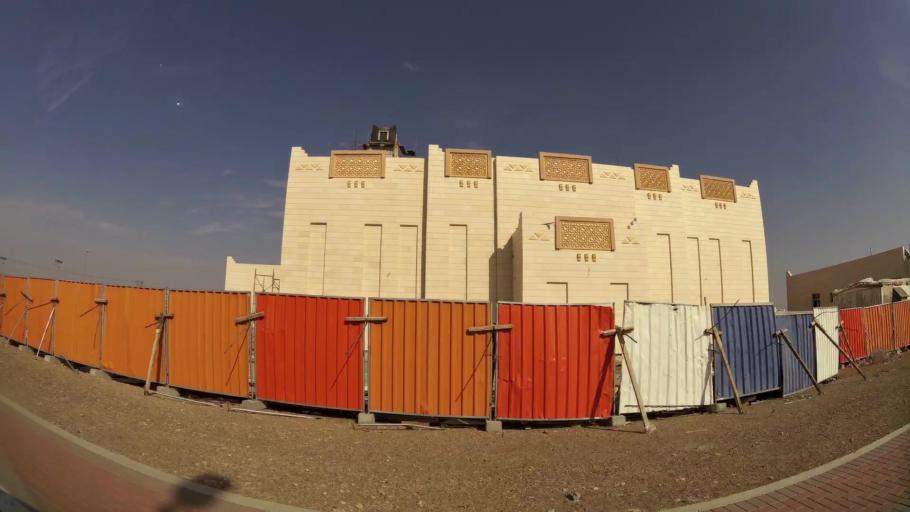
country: AE
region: Abu Dhabi
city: Al Ain
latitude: 24.0900
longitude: 55.8648
